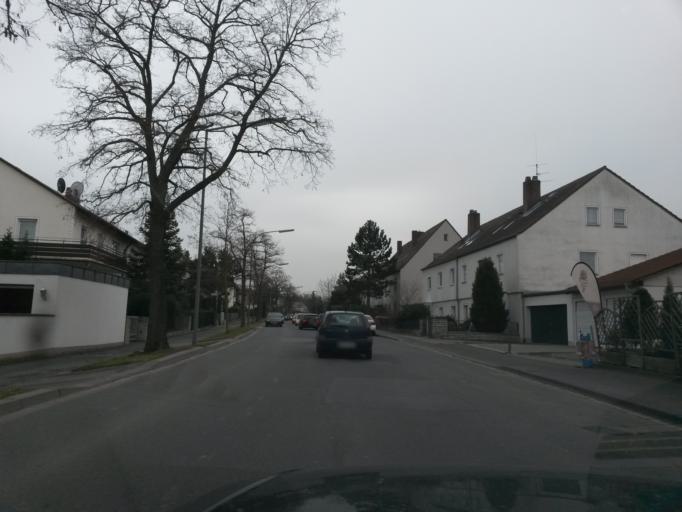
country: DE
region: Bavaria
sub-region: Regierungsbezirk Unterfranken
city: Wuerzburg
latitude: 49.7906
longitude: 9.9588
